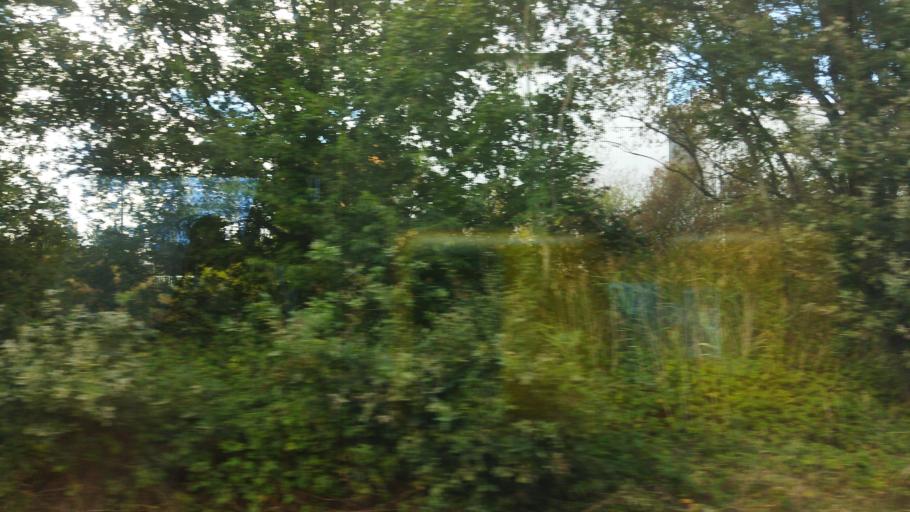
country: DE
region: Lower Saxony
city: Papenburg
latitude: 53.0965
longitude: 7.3964
